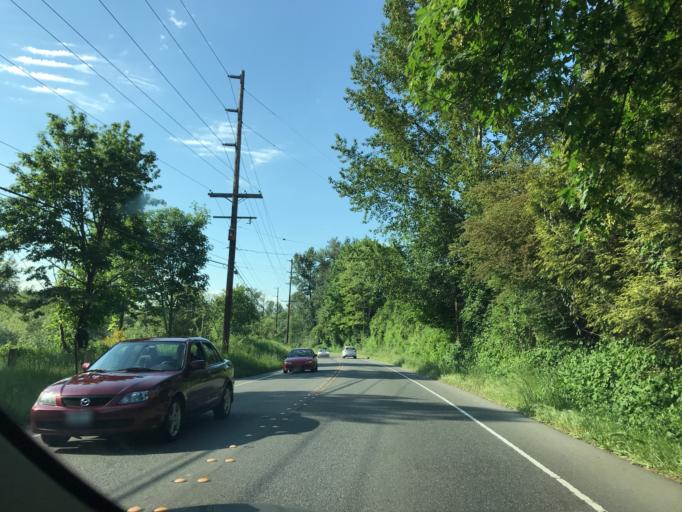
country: US
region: Washington
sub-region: King County
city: Issaquah
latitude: 47.5121
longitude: -122.0234
